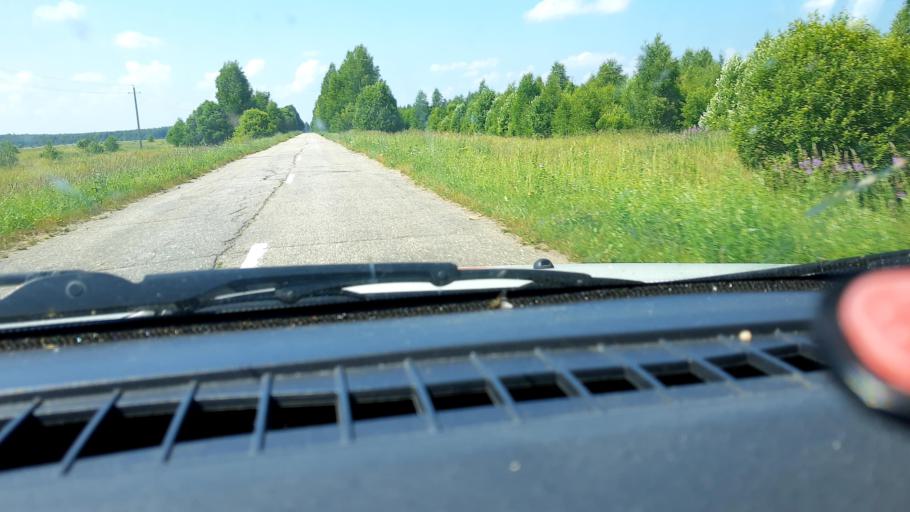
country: RU
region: Nizjnij Novgorod
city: Sharanga
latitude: 57.0657
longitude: 46.6662
